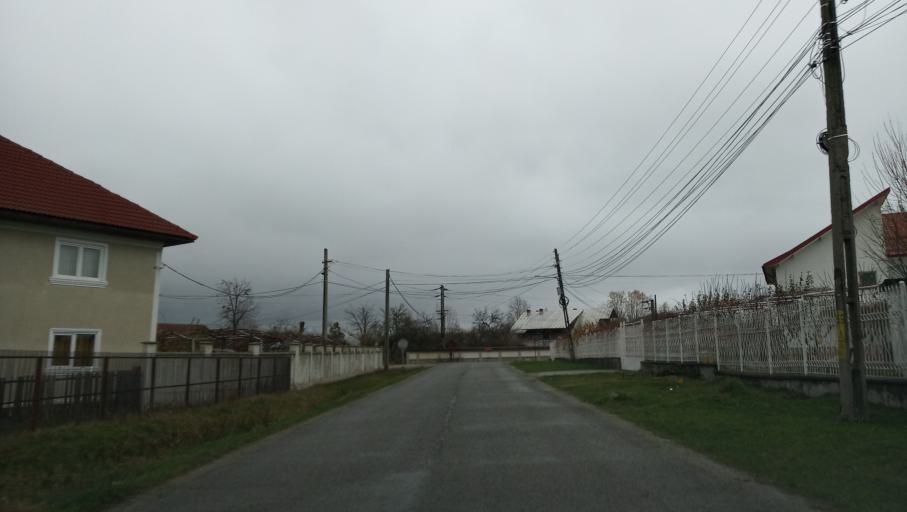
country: RO
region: Gorj
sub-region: Novaci
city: Pociovalistea
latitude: 45.1517
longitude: 23.6240
